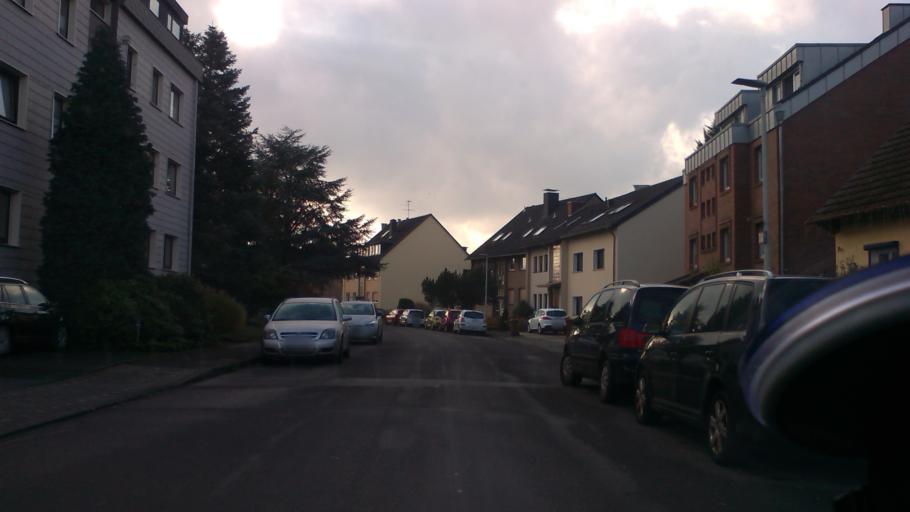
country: DE
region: North Rhine-Westphalia
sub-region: Regierungsbezirk Dusseldorf
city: Hilden
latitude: 51.1589
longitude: 6.9362
